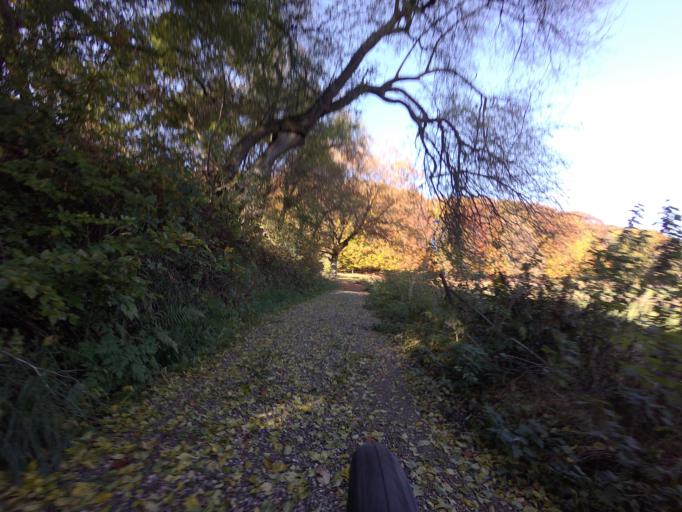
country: DK
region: Central Jutland
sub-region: Syddjurs Kommune
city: Ryomgard
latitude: 56.4493
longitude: 10.6180
